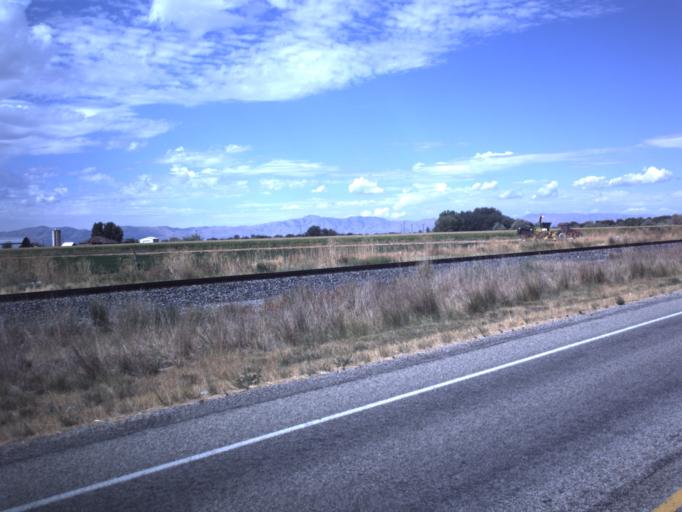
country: US
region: Utah
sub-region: Box Elder County
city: Brigham City
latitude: 41.5414
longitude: -112.0864
